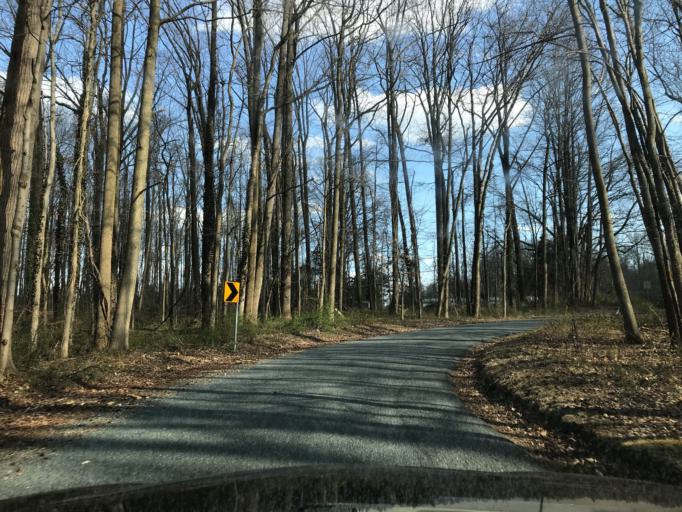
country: US
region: Maryland
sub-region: Harford County
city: Riverside
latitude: 39.4448
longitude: -76.2299
